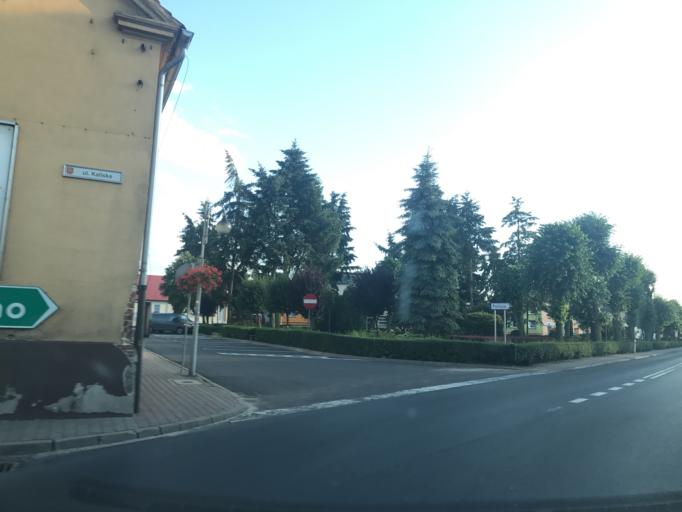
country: PL
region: Greater Poland Voivodeship
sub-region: Powiat jarocinski
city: Jaraczewo
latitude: 51.9694
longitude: 17.2990
